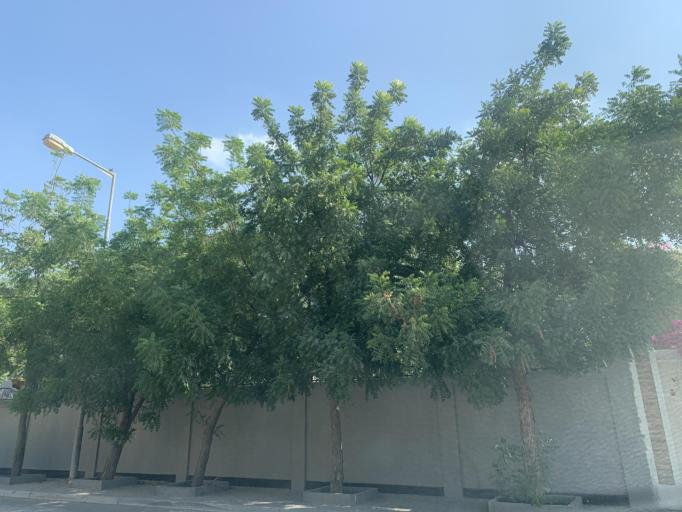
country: BH
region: Central Governorate
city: Madinat Hamad
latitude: 26.1279
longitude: 50.5052
